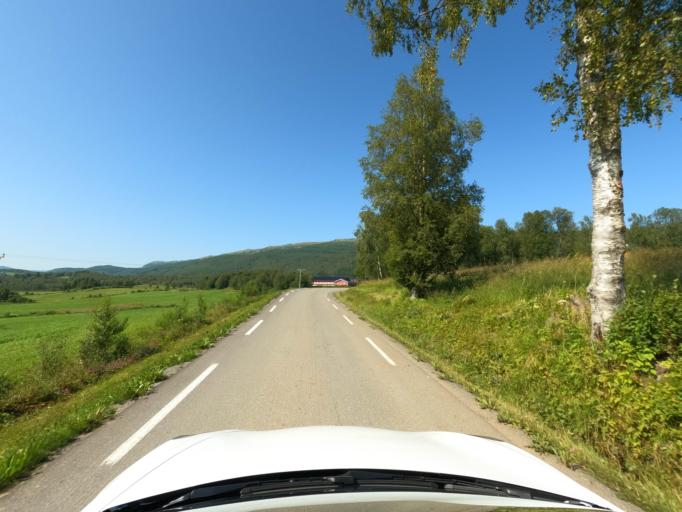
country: NO
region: Nordland
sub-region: Ballangen
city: Ballangen
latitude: 68.3453
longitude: 16.8085
